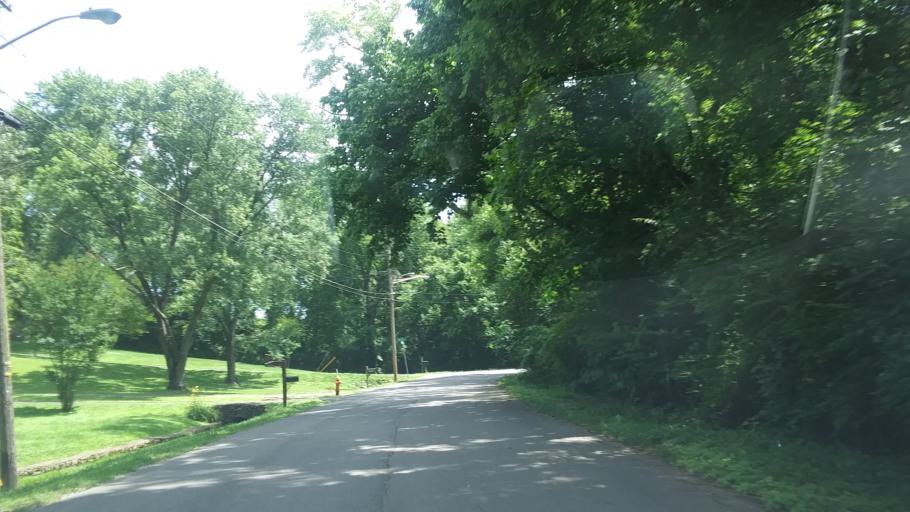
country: US
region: Tennessee
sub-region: Davidson County
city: Oak Hill
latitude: 36.0723
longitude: -86.7132
